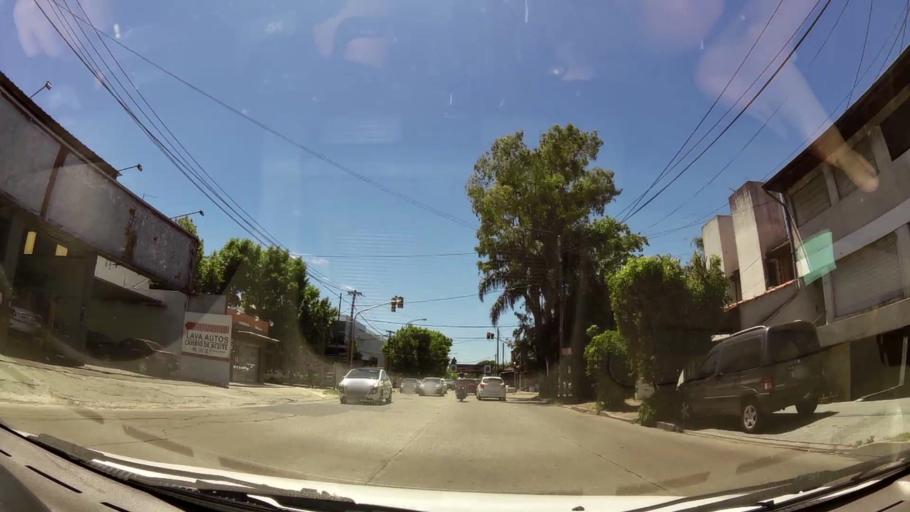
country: AR
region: Buenos Aires
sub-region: Partido de San Isidro
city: San Isidro
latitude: -34.5065
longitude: -58.5288
